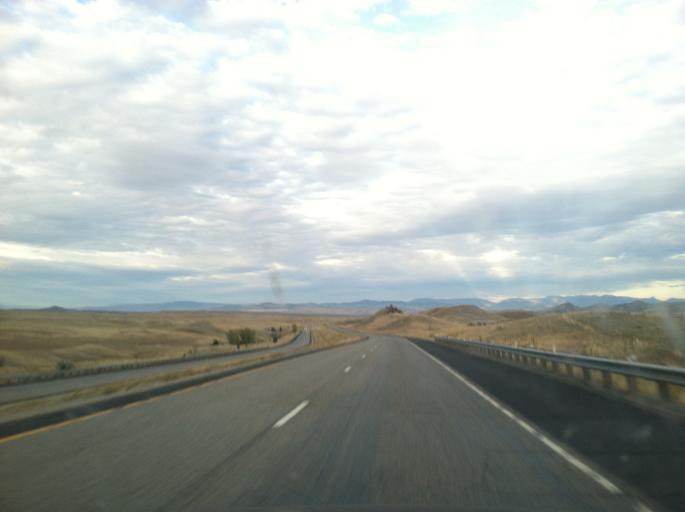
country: US
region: Montana
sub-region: Jefferson County
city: Whitehall
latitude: 45.8981
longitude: -111.8261
